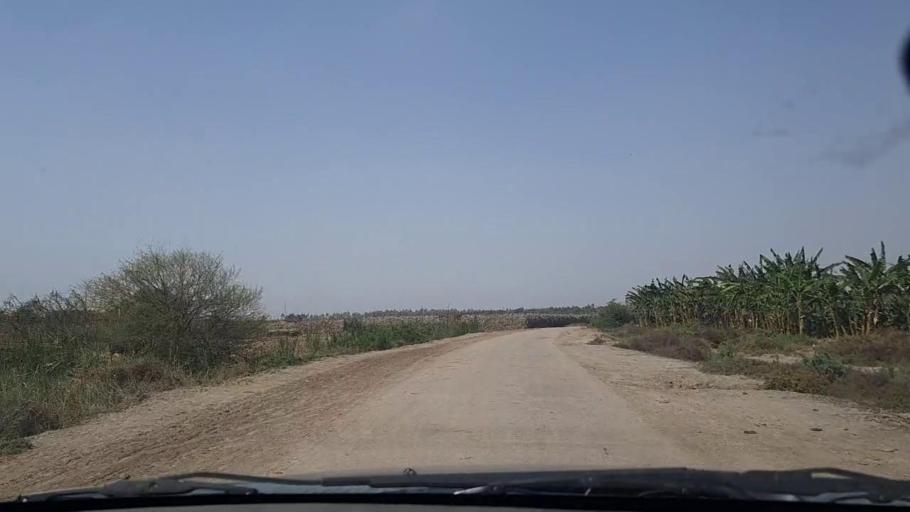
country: PK
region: Sindh
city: Keti Bandar
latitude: 24.2757
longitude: 67.6728
